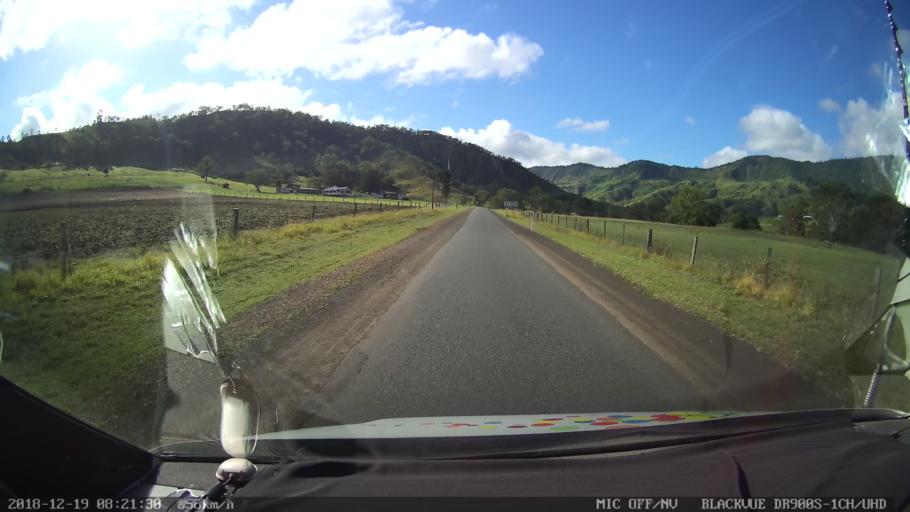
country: AU
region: New South Wales
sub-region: Kyogle
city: Kyogle
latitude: -28.2975
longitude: 152.9101
